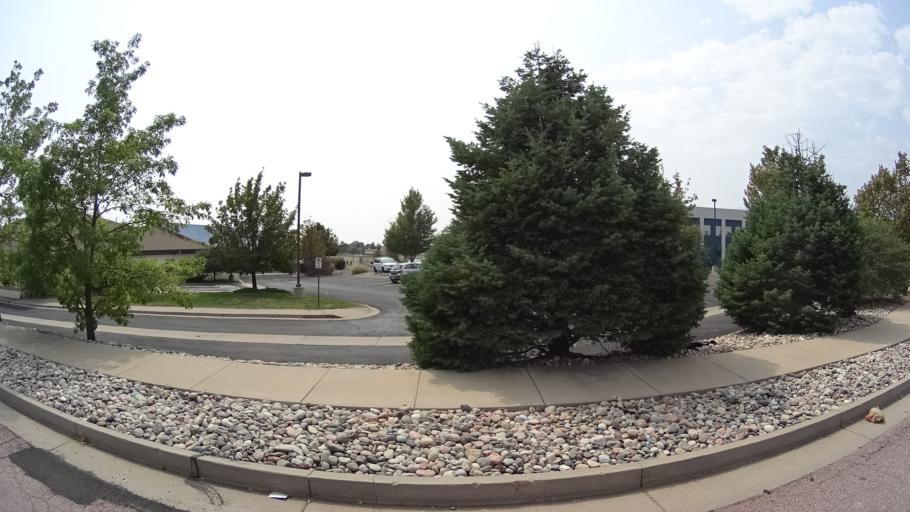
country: US
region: Colorado
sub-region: El Paso County
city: Colorado Springs
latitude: 38.8312
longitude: -104.7863
